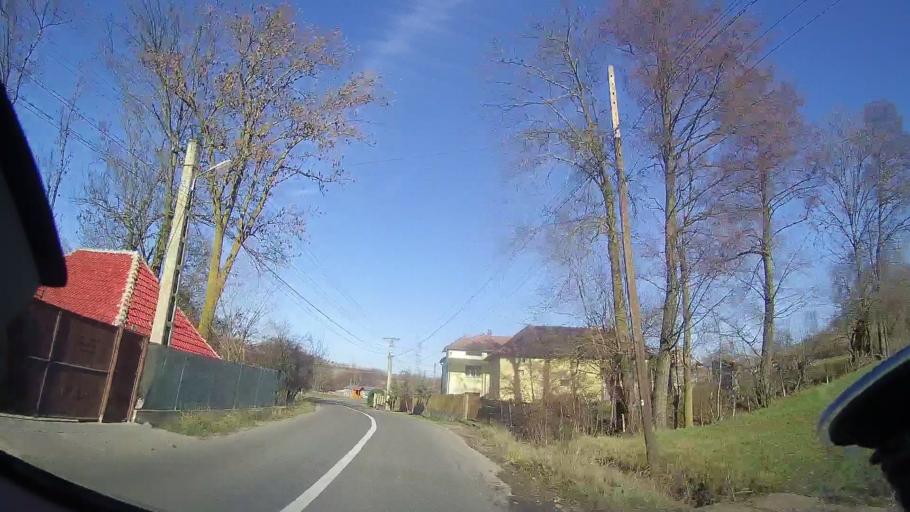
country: RO
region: Bihor
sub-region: Comuna Bratca
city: Bratca
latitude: 46.9411
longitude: 22.6046
